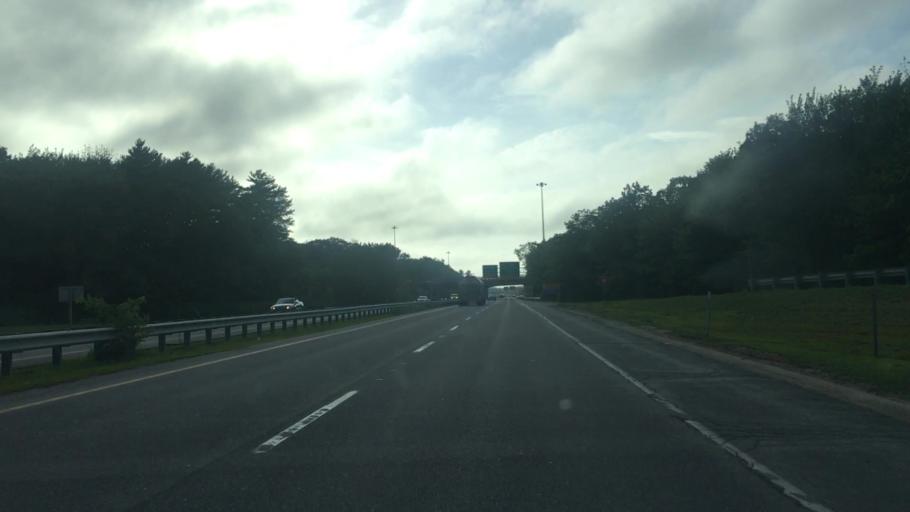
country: US
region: Maine
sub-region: Cumberland County
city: South Portland Gardens
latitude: 43.6258
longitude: -70.3254
